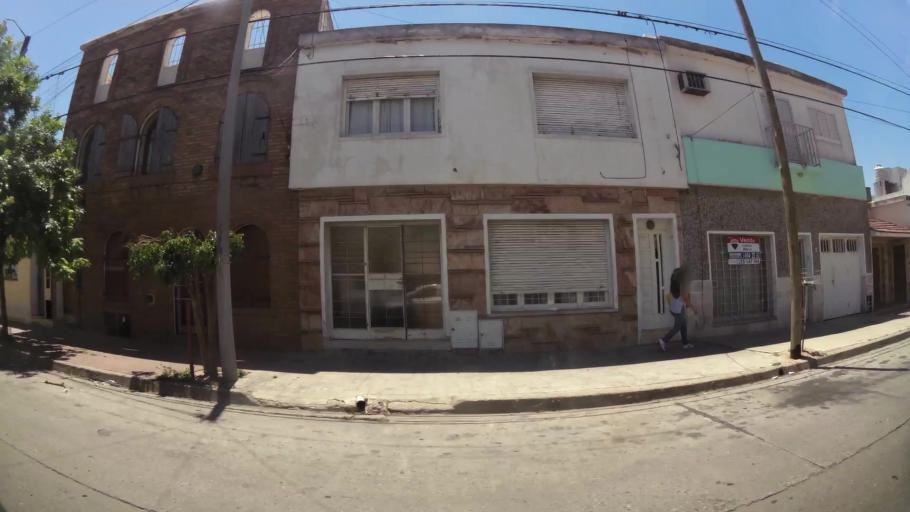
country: AR
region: Cordoba
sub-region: Departamento de Capital
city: Cordoba
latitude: -31.4019
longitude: -64.2183
